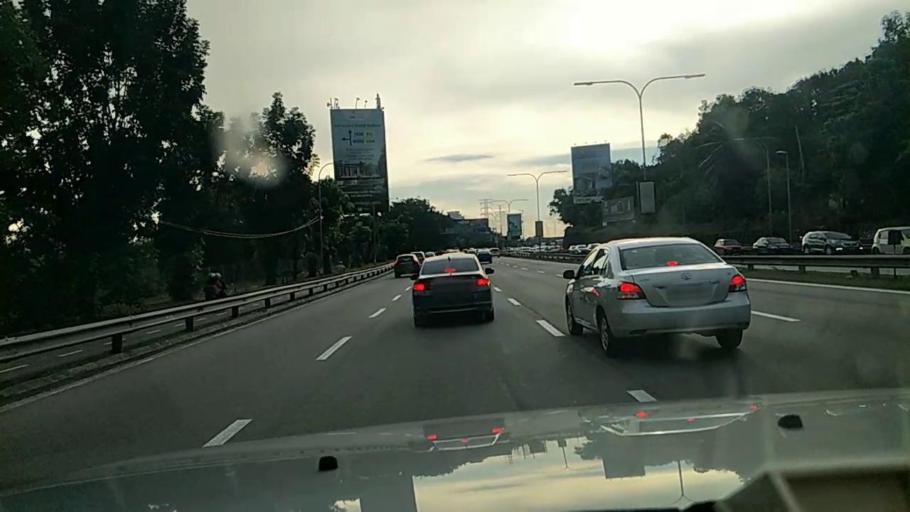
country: MY
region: Selangor
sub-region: Petaling
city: Petaling Jaya
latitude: 3.0832
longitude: 101.6033
